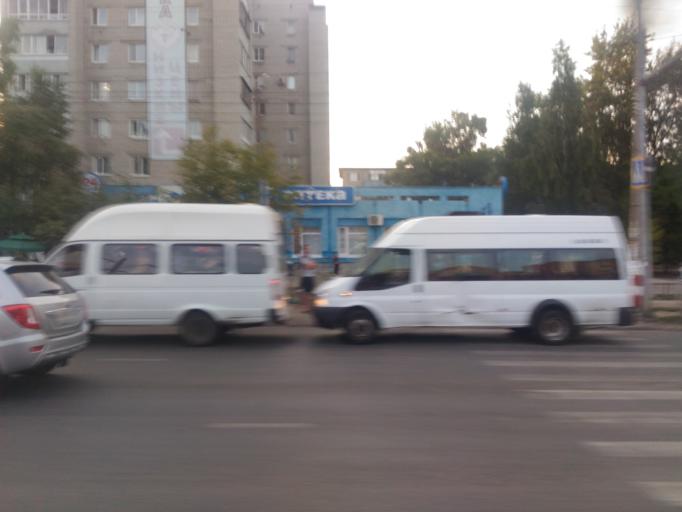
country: RU
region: Ulyanovsk
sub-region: Ulyanovskiy Rayon
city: Ulyanovsk
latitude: 54.2781
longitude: 48.2932
